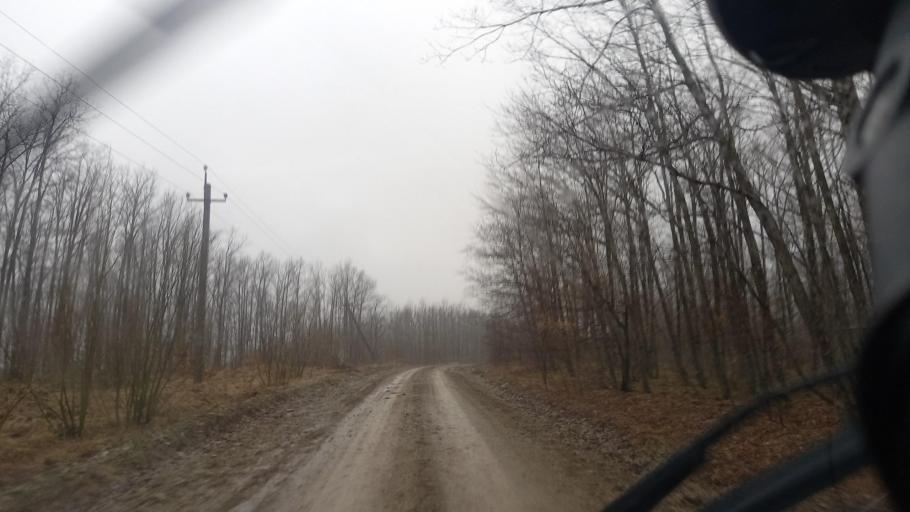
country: RU
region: Krasnodarskiy
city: Saratovskaya
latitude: 44.6181
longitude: 39.2527
